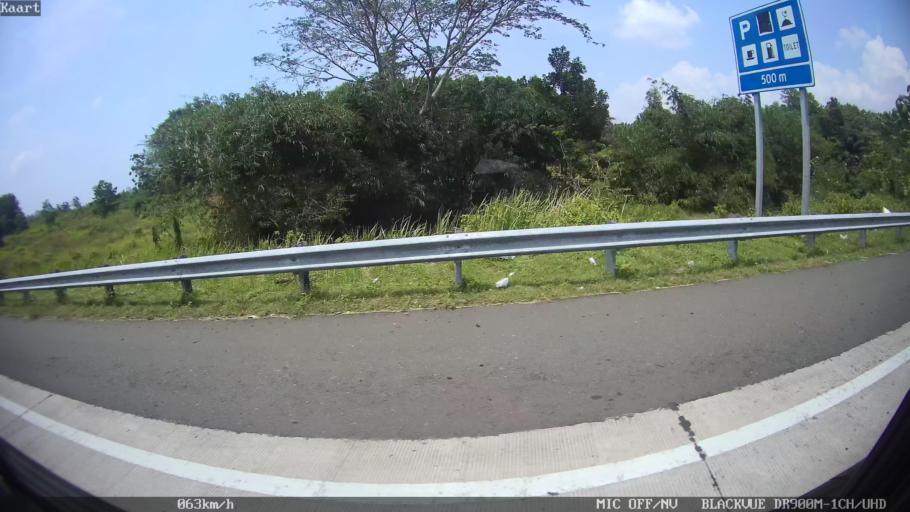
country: ID
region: Lampung
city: Kedaton
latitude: -5.3221
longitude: 105.2735
